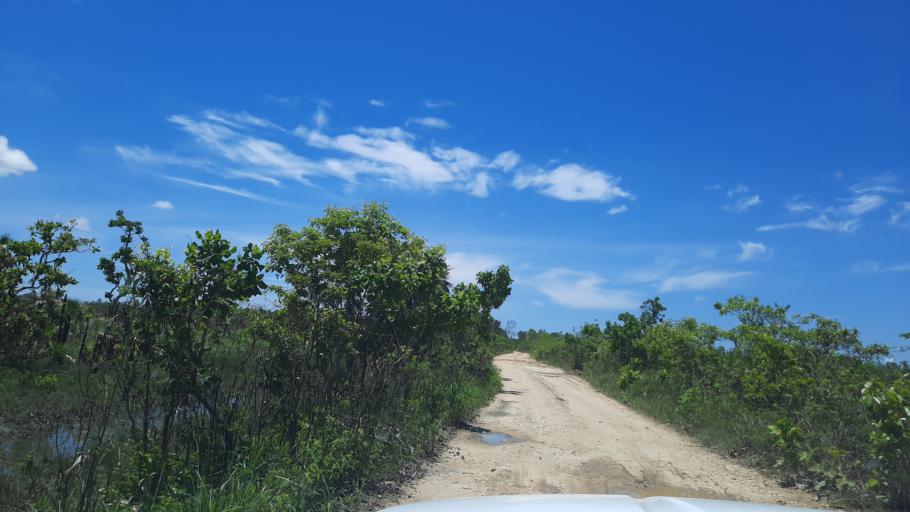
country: BZ
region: Cayo
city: Belmopan
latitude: 17.3793
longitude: -88.4903
